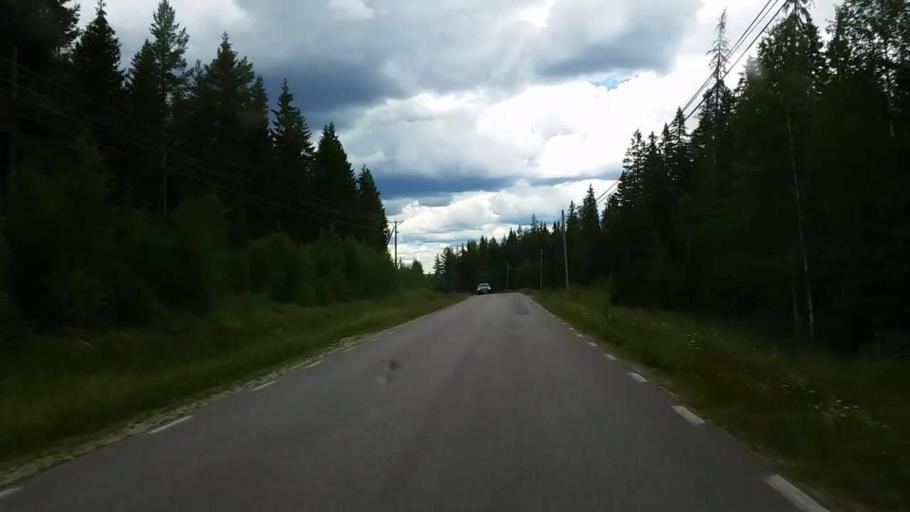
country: SE
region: Gaevleborg
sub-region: Ovanakers Kommun
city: Edsbyn
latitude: 61.4309
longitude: 15.8989
